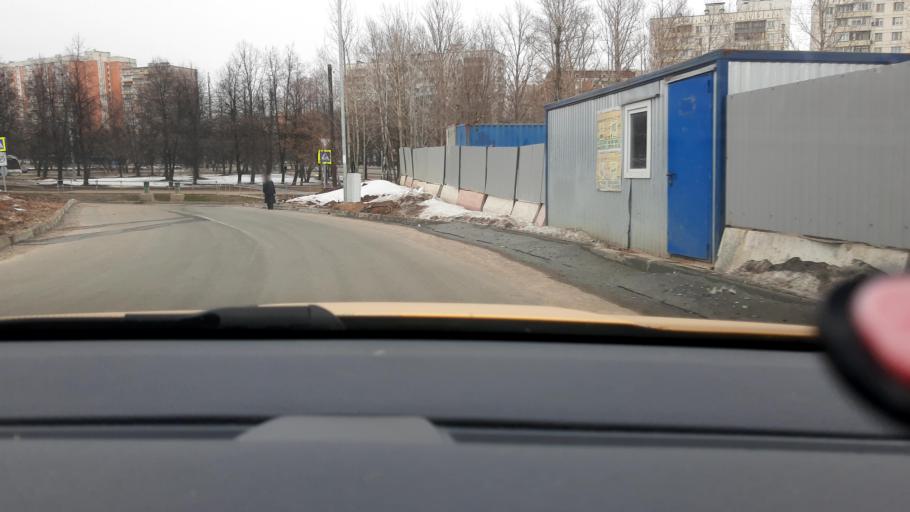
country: RU
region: Moscow
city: Kozeyevo
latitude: 55.8864
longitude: 37.6417
